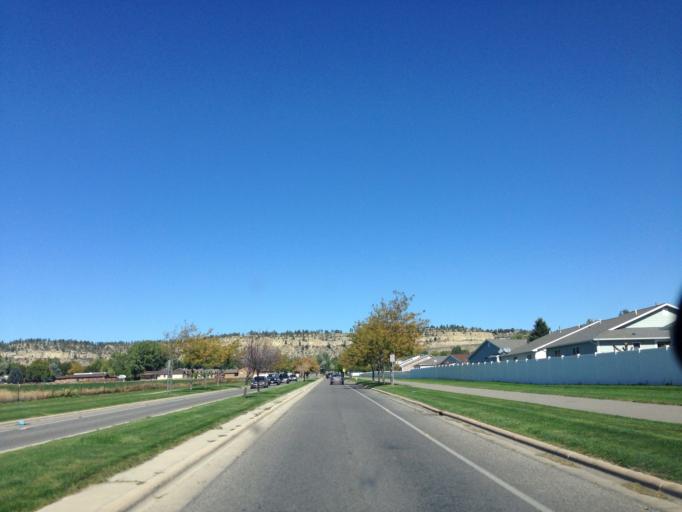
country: US
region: Montana
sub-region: Yellowstone County
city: Billings
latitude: 45.7884
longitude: -108.6007
